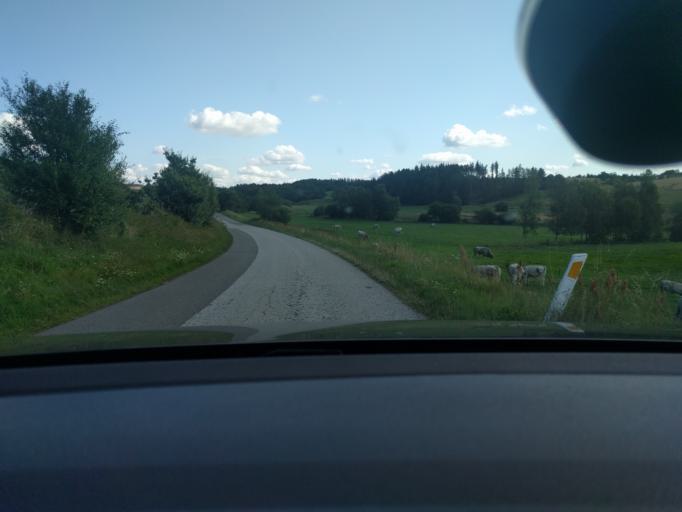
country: DK
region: Central Jutland
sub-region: Viborg Kommune
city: Viborg
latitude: 56.5149
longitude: 9.3147
